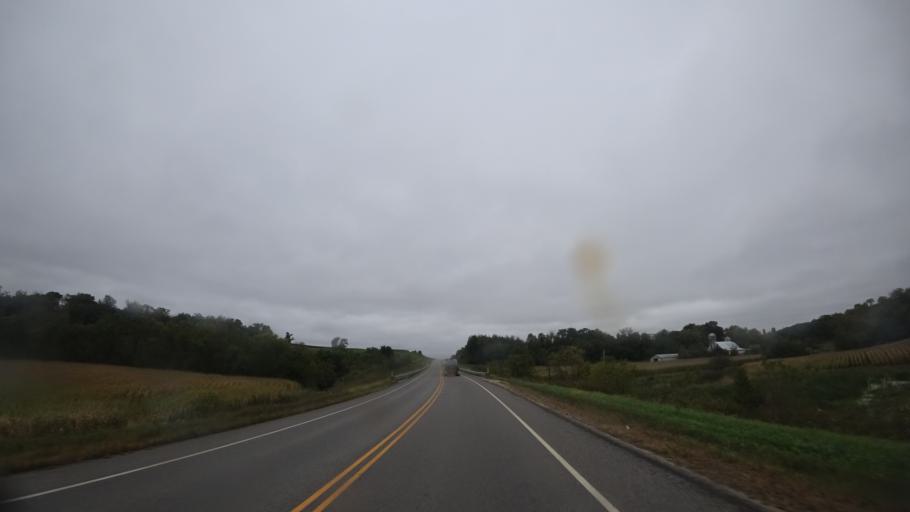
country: US
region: Wisconsin
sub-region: Crawford County
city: Prairie du Chien
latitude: 43.0239
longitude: -91.0286
